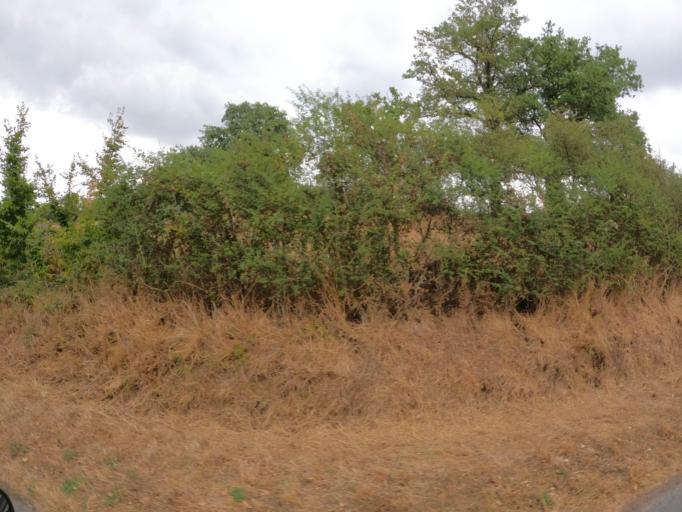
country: FR
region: Pays de la Loire
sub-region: Departement de Maine-et-Loire
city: Le Longeron
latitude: 46.9980
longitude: -1.0701
